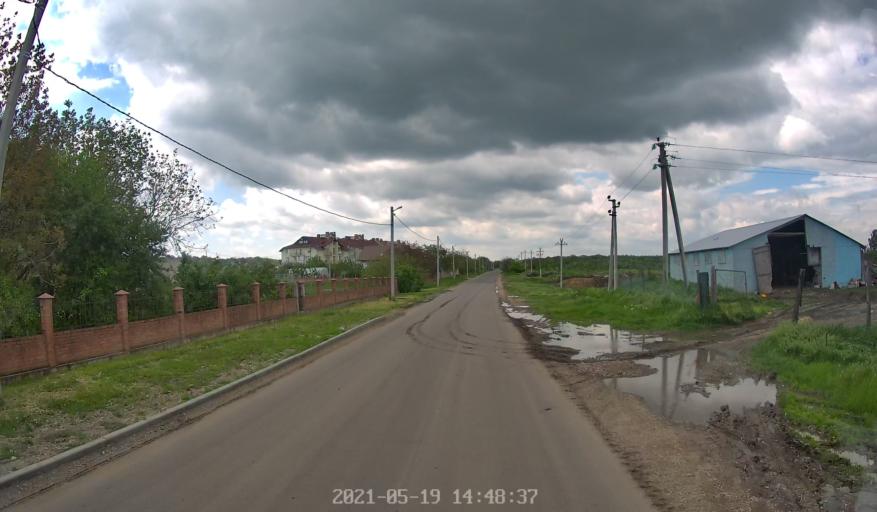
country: MD
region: Chisinau
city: Stauceni
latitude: 47.0457
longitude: 28.9592
